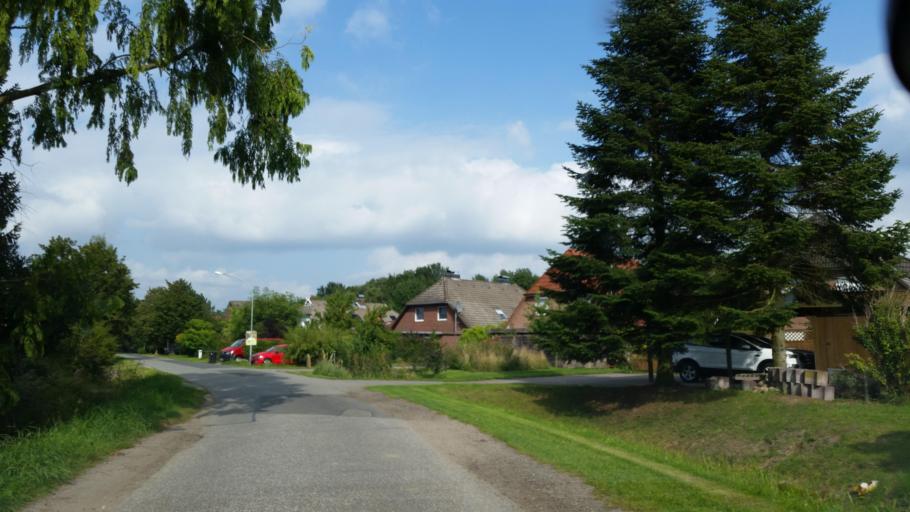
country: DE
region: Lower Saxony
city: Marschacht
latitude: 53.4129
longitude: 10.3302
